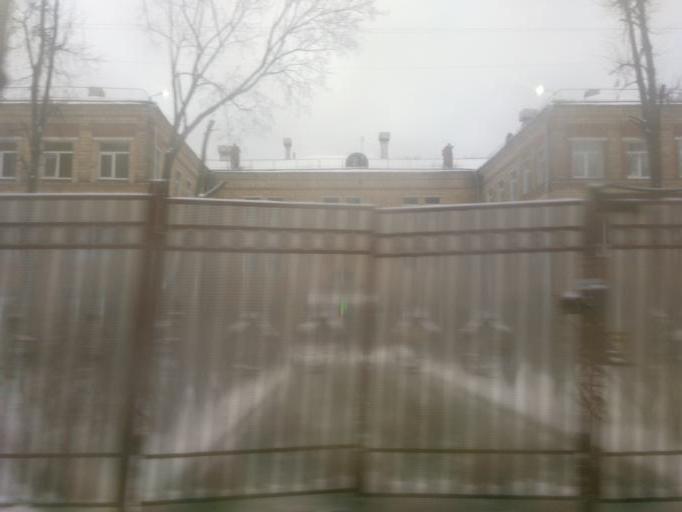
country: RU
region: Moskovskaya
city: Semenovskoye
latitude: 55.6918
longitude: 37.5473
